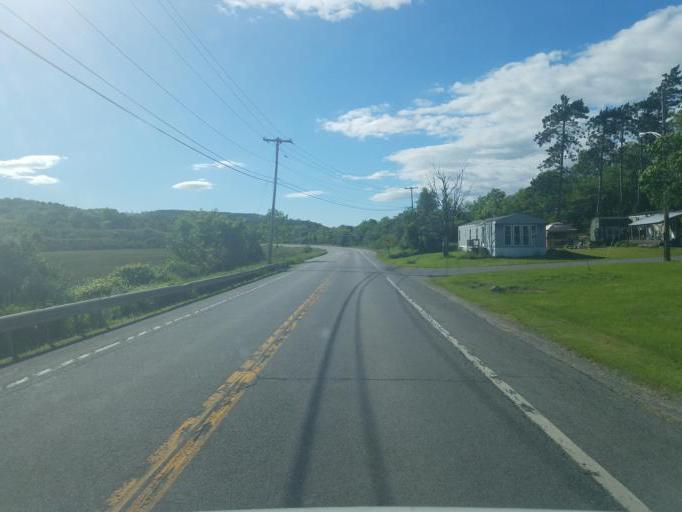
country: US
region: New York
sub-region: Herkimer County
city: Little Falls
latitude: 43.0188
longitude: -74.8137
